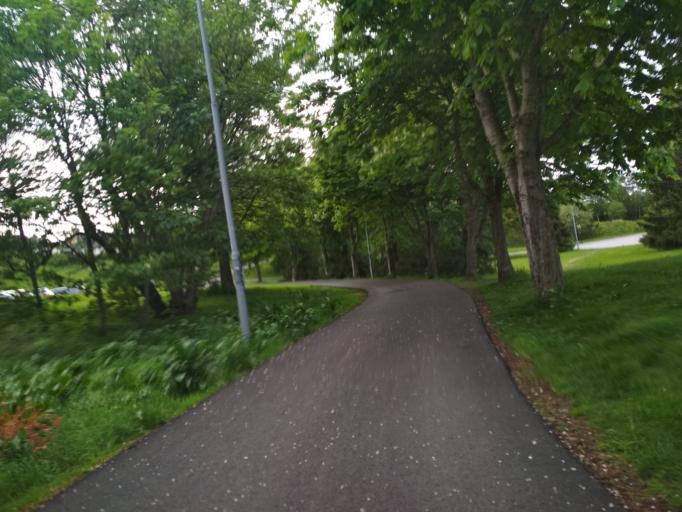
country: NO
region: Rogaland
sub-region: Stavanger
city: Stavanger
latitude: 58.9499
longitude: 5.7184
